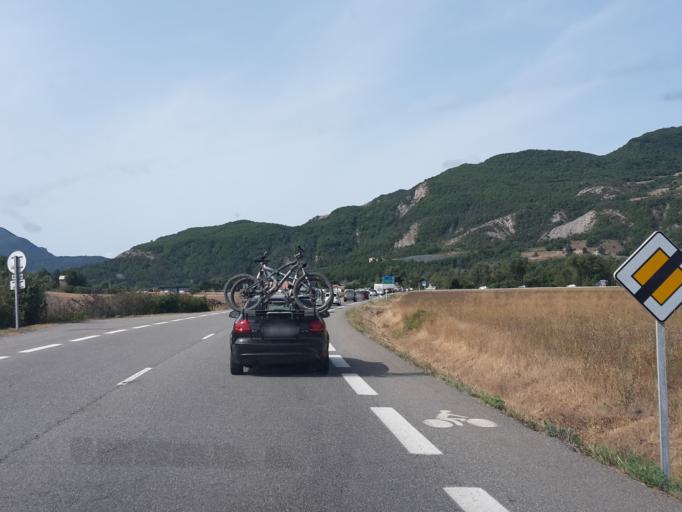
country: FR
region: Provence-Alpes-Cote d'Azur
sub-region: Departement des Hautes-Alpes
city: Tallard
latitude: 44.4496
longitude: 6.0365
